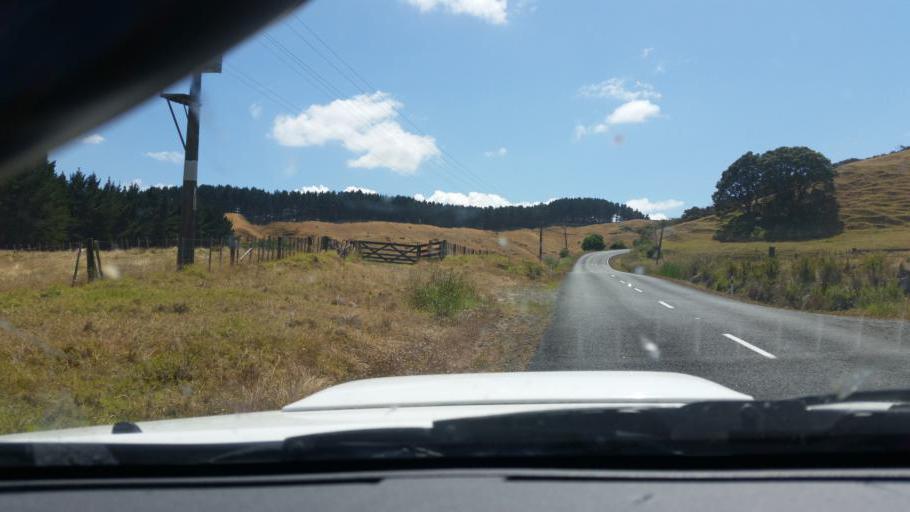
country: NZ
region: Northland
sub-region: Kaipara District
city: Dargaville
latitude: -35.8226
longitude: 173.6814
